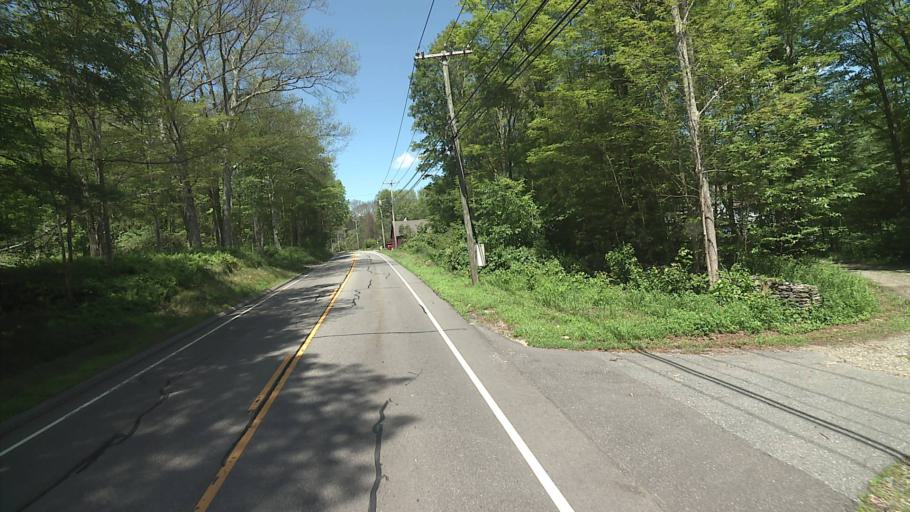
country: US
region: Connecticut
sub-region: Windham County
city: Plainfield Village
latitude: 41.7035
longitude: -72.0078
